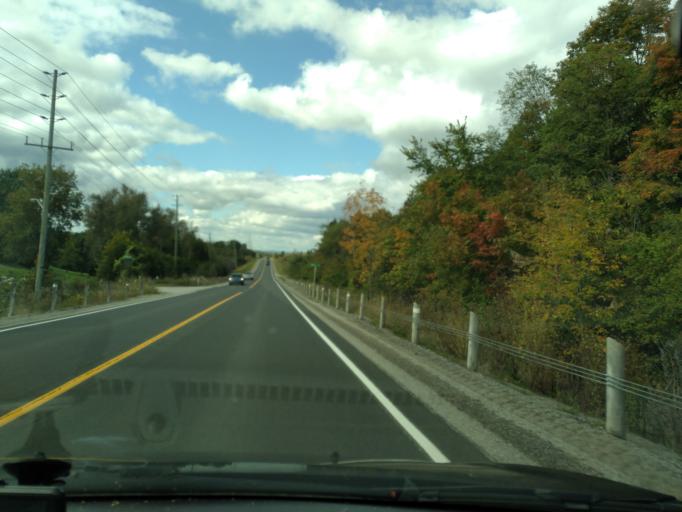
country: CA
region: Ontario
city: Innisfil
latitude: 44.2626
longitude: -79.7594
